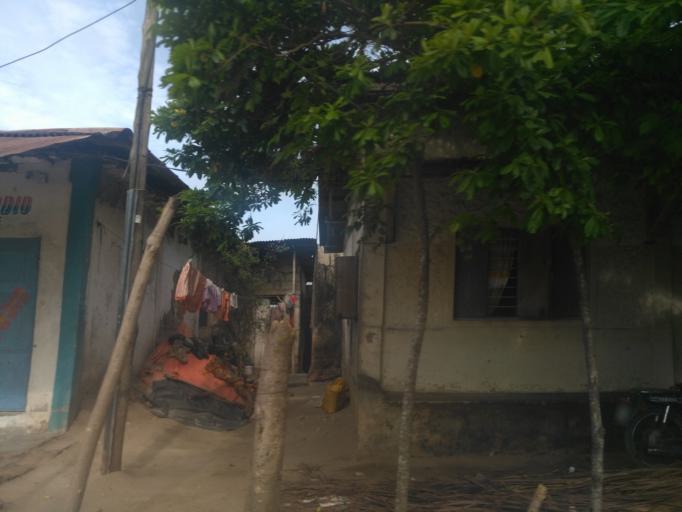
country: TZ
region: Zanzibar Urban/West
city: Zanzibar
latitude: -6.1688
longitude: 39.2094
